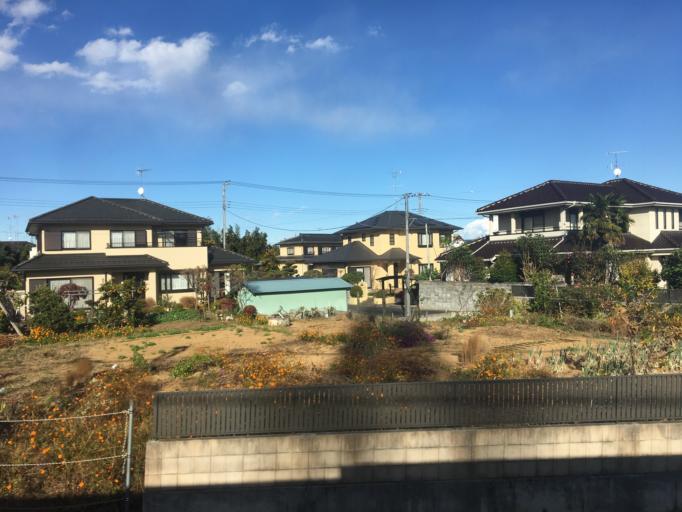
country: JP
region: Saitama
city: Ogawa
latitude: 36.0432
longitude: 139.3308
